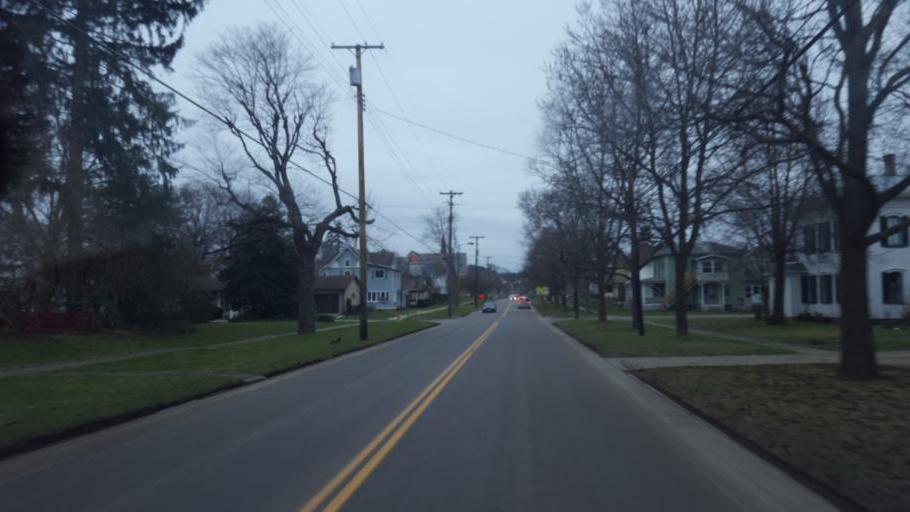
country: US
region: Ohio
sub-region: Ashland County
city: Loudonville
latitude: 40.6355
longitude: -82.2282
